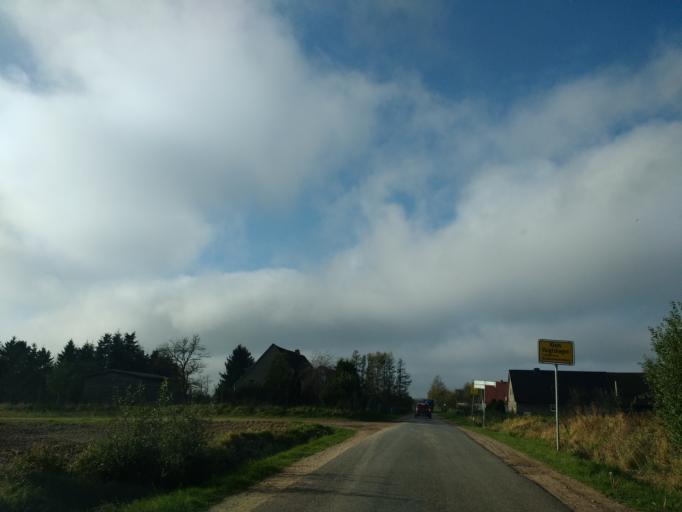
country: DE
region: Mecklenburg-Vorpommern
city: Kalkhorst
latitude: 53.9363
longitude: 11.0360
